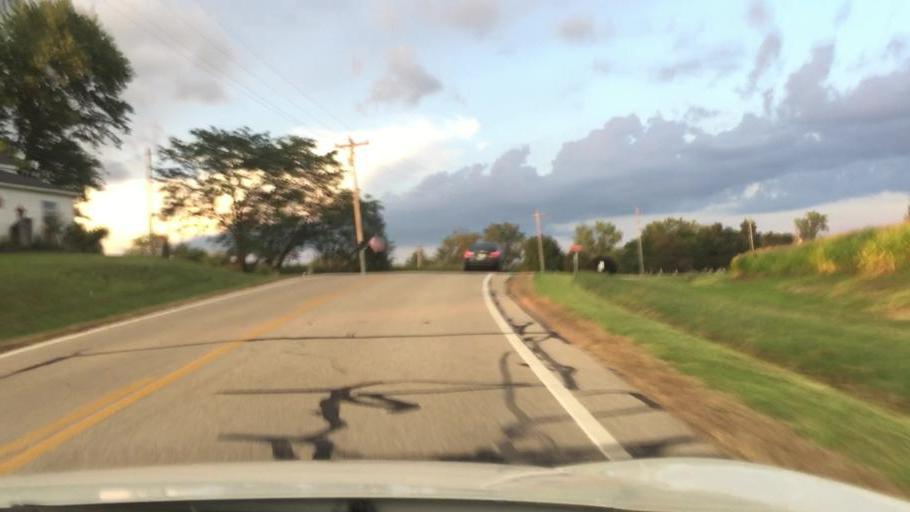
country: US
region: Ohio
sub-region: Champaign County
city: Mechanicsburg
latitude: 40.0242
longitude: -83.5798
